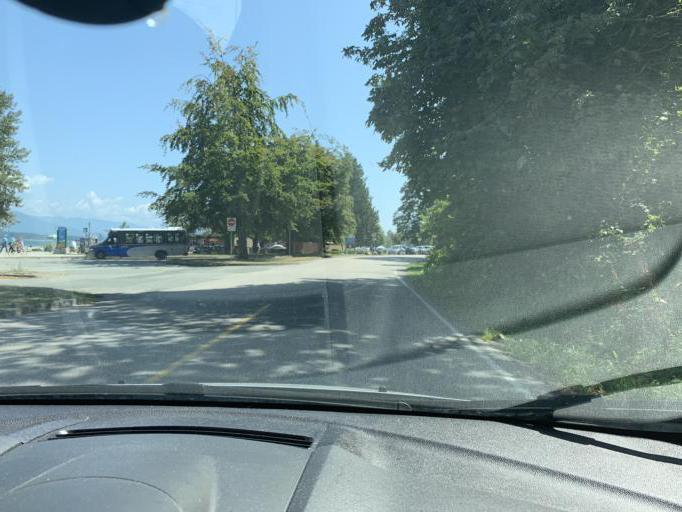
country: CA
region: British Columbia
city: West End
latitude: 49.2762
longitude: -123.2161
